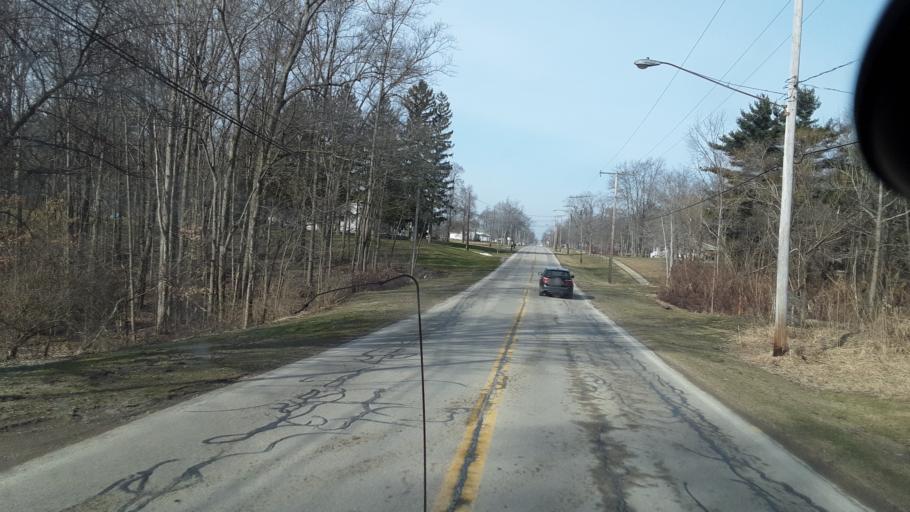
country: US
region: Ohio
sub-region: Ashtabula County
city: Jefferson
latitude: 41.7383
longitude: -80.7505
